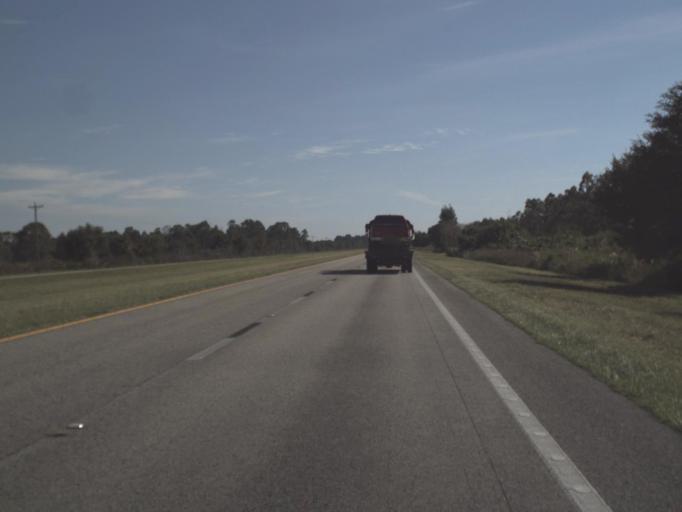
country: US
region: Florida
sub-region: Hendry County
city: Port LaBelle
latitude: 26.9844
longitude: -81.3229
